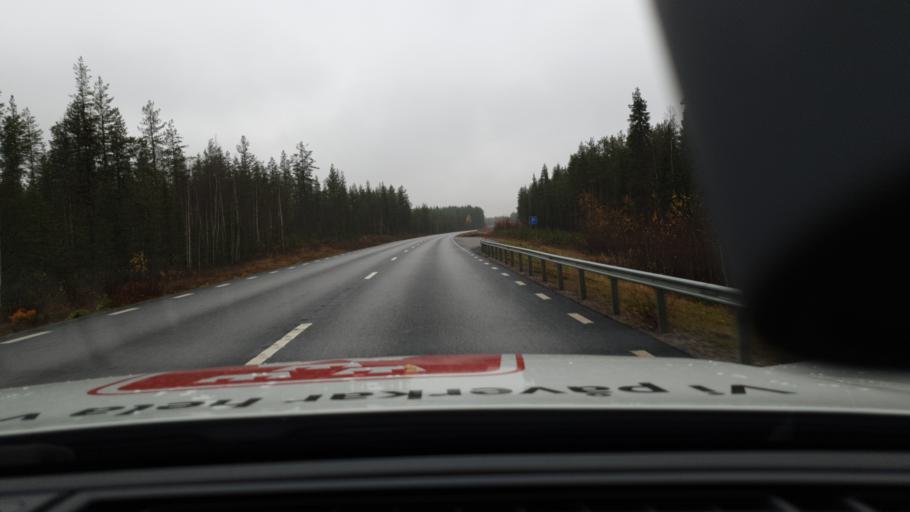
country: SE
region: Norrbotten
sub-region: Overkalix Kommun
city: OEverkalix
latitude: 66.6330
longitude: 22.2071
